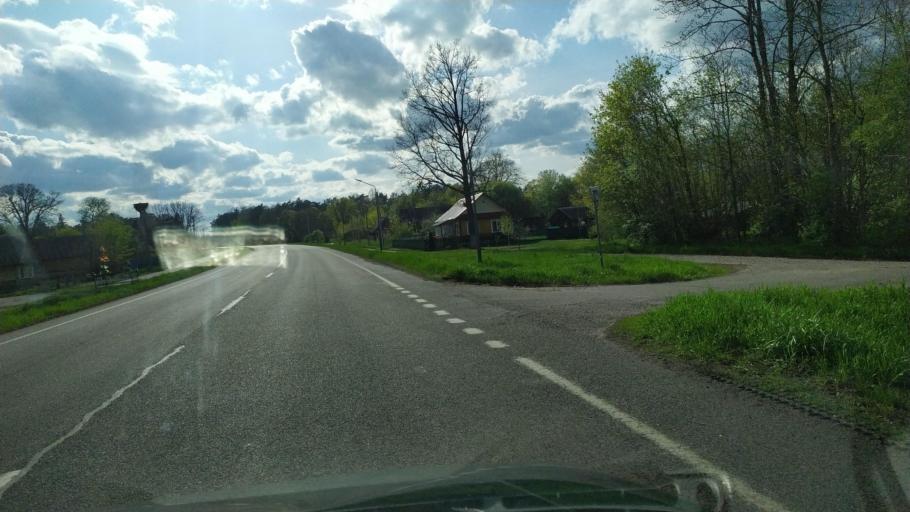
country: BY
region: Brest
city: Pruzhany
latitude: 52.7036
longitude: 24.3185
